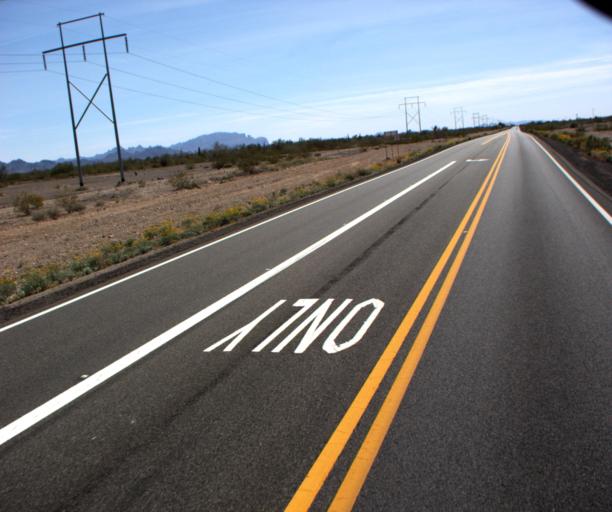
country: US
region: Arizona
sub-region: La Paz County
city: Quartzsite
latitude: 33.5799
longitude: -114.2171
